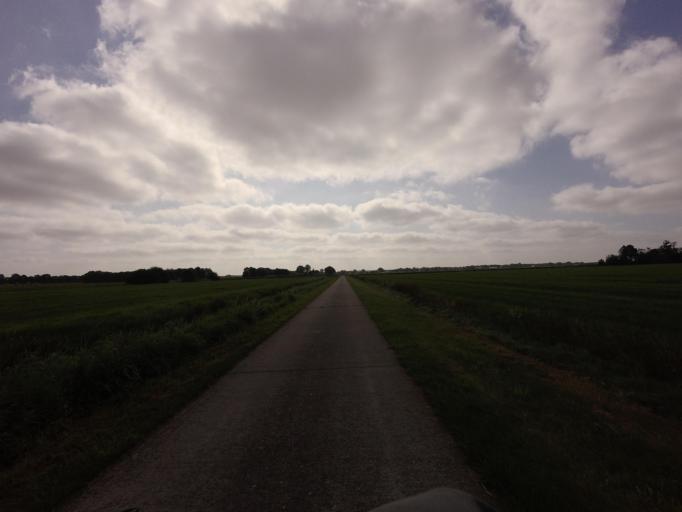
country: NL
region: Overijssel
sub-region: Gemeente Steenwijkerland
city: Steenwijk
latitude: 52.8123
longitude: 6.1759
